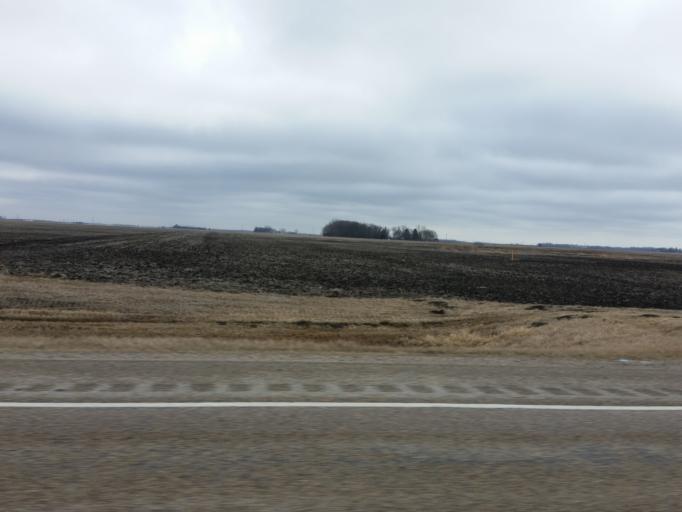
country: US
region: North Dakota
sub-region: Cass County
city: Casselton
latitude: 46.8689
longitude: -97.2108
